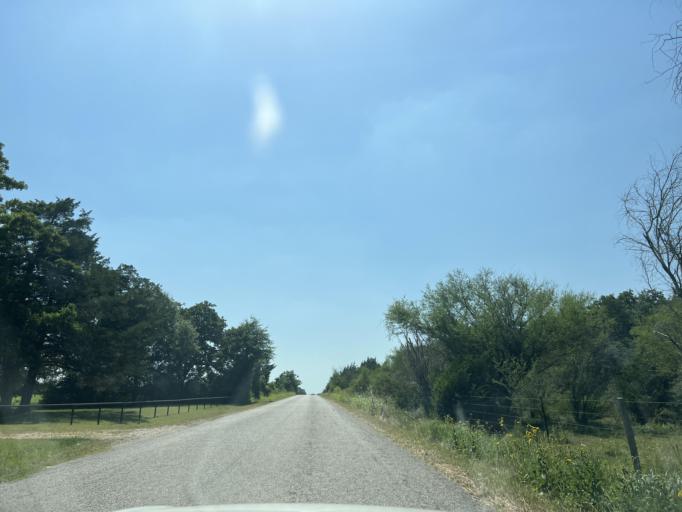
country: US
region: Texas
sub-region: Washington County
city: Brenham
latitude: 30.1534
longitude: -96.4787
